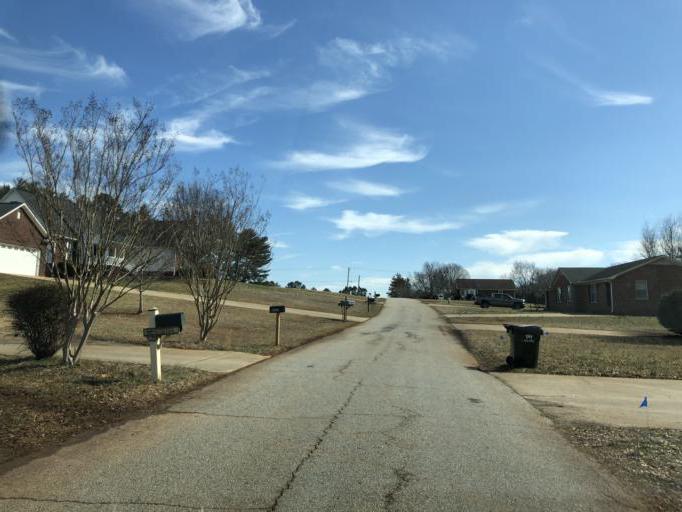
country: US
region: South Carolina
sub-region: Spartanburg County
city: Boiling Springs
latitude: 35.0392
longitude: -81.9474
